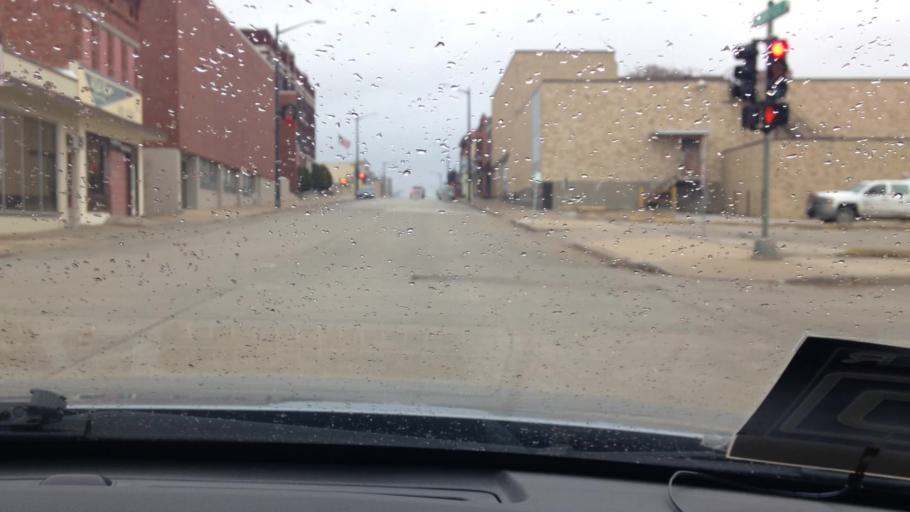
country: US
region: Kansas
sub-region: Leavenworth County
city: Leavenworth
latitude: 39.3180
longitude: -94.9187
